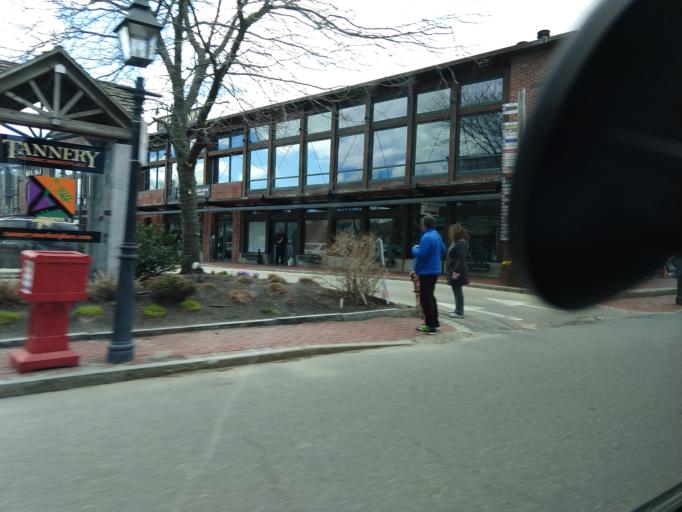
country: US
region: Massachusetts
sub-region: Essex County
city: Newburyport
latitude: 42.8108
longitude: -70.8657
